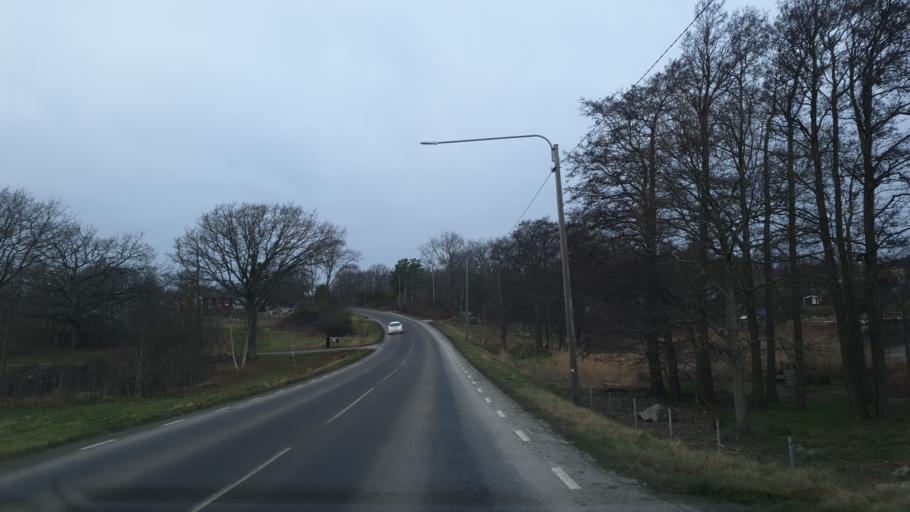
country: SE
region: Blekinge
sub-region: Karlskrona Kommun
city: Sturko
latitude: 56.1111
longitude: 15.7074
